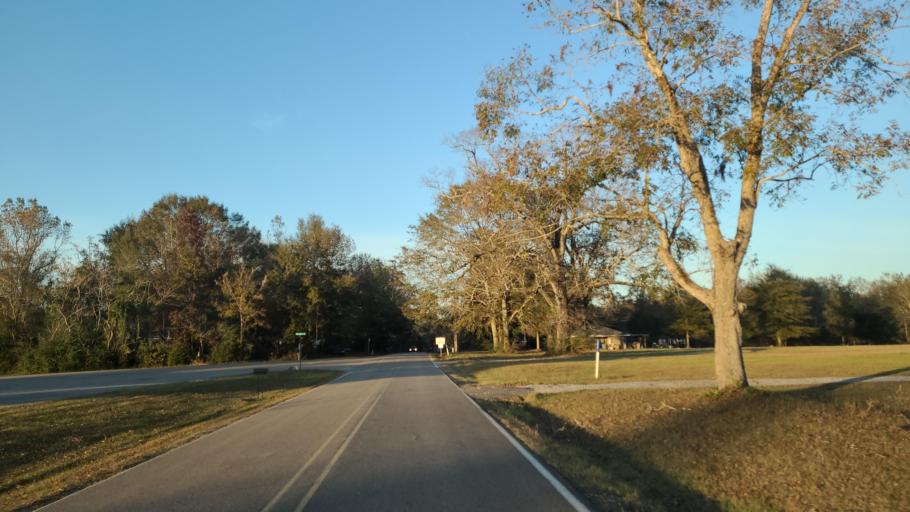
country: US
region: Mississippi
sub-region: Stone County
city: Wiggins
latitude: 30.9929
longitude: -89.2595
